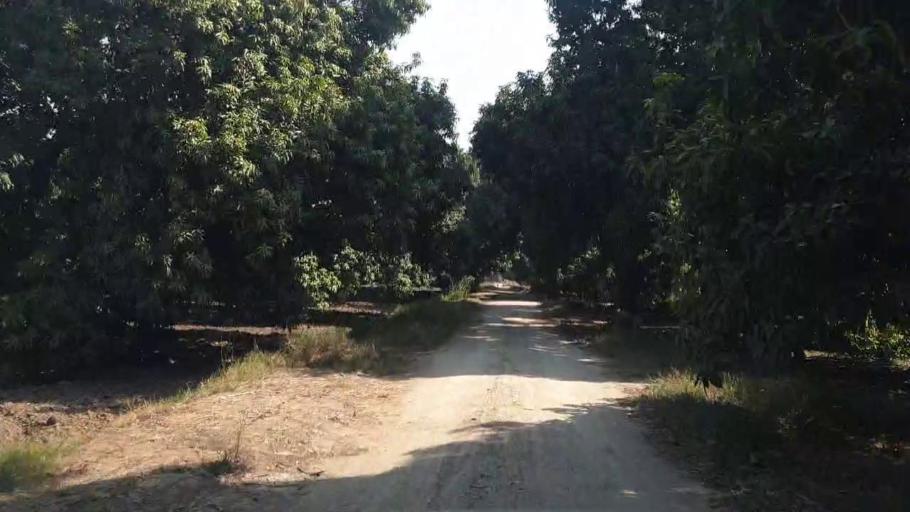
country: PK
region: Sindh
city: Tando Jam
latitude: 25.3445
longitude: 68.6153
